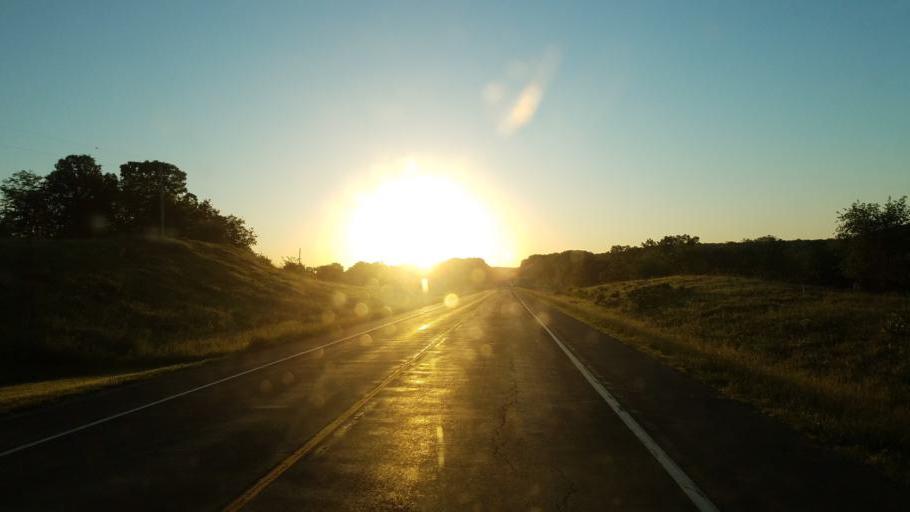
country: US
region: Missouri
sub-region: Schuyler County
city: Lancaster
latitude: 40.4869
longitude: -92.6282
